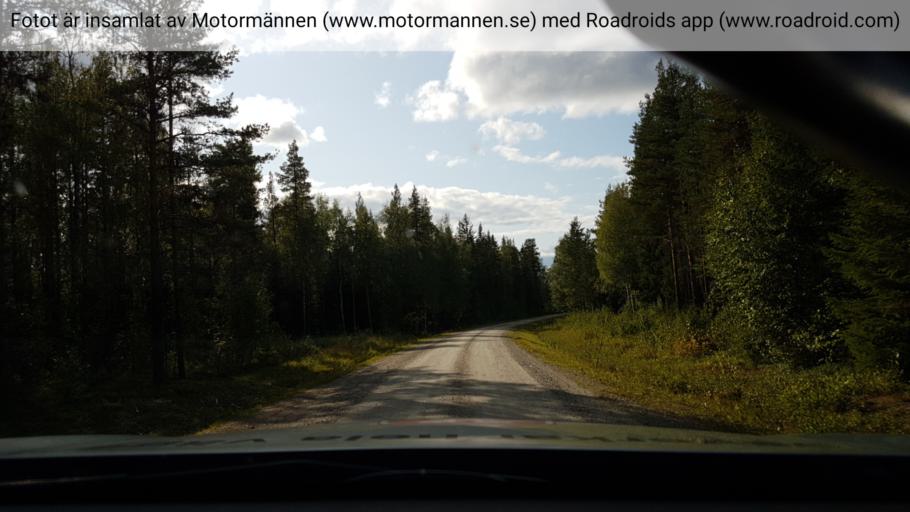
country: SE
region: Vaesterbotten
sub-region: Lycksele Kommun
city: Lycksele
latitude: 64.7278
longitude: 19.0659
